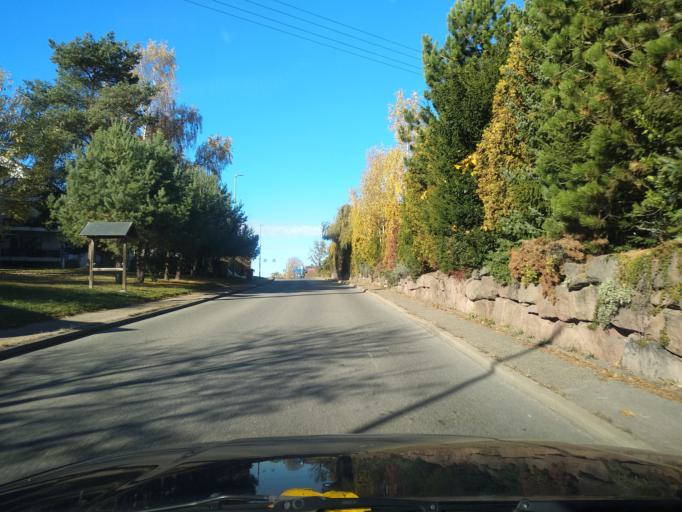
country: DE
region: Baden-Wuerttemberg
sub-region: Karlsruhe Region
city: Bad Liebenzell
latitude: 48.7689
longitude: 8.7530
